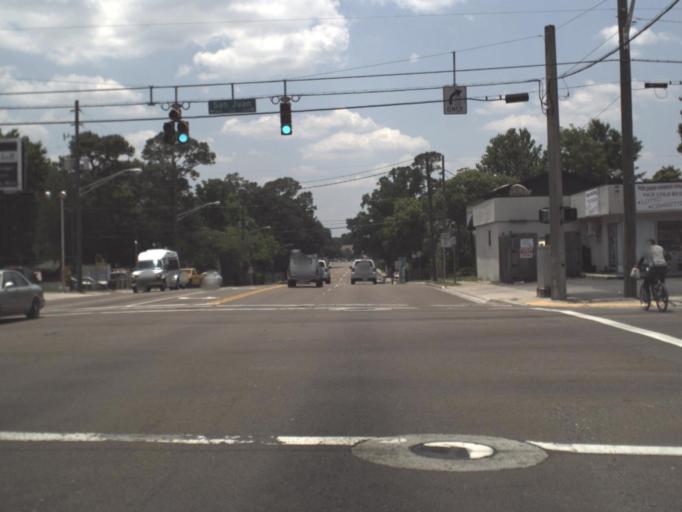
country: US
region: Florida
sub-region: Duval County
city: Jacksonville
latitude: 30.2823
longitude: -81.7304
